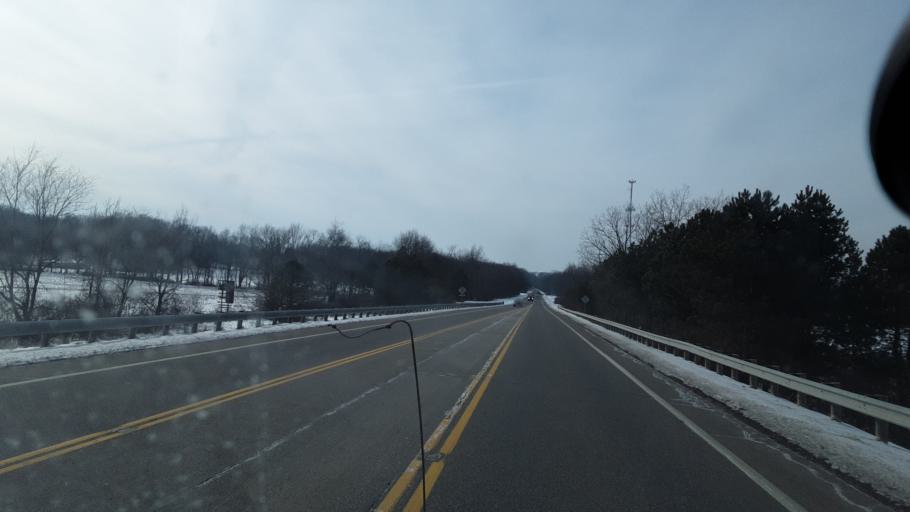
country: US
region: Ohio
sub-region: Summit County
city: Mogadore
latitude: 41.0276
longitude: -81.3847
